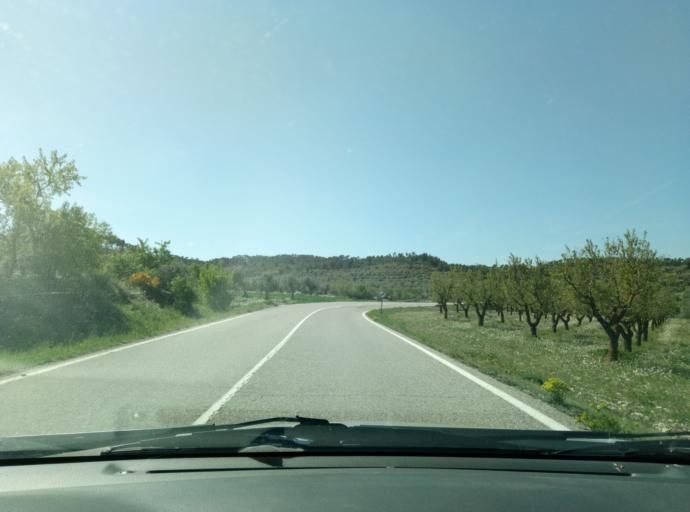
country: ES
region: Catalonia
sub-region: Provincia de Lleida
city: Vallbona de les Monges
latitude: 41.5367
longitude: 1.0264
